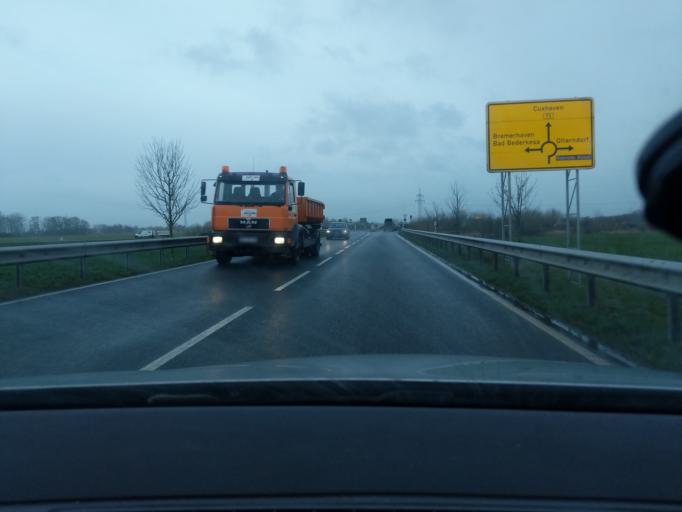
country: DE
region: Lower Saxony
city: Otterndorf
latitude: 53.7958
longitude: 8.8953
